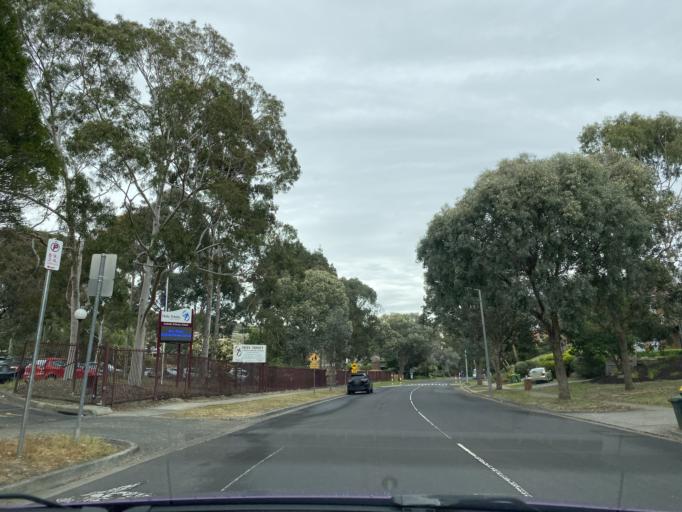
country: AU
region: Victoria
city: Saint Helena
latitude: -37.6976
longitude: 145.1356
